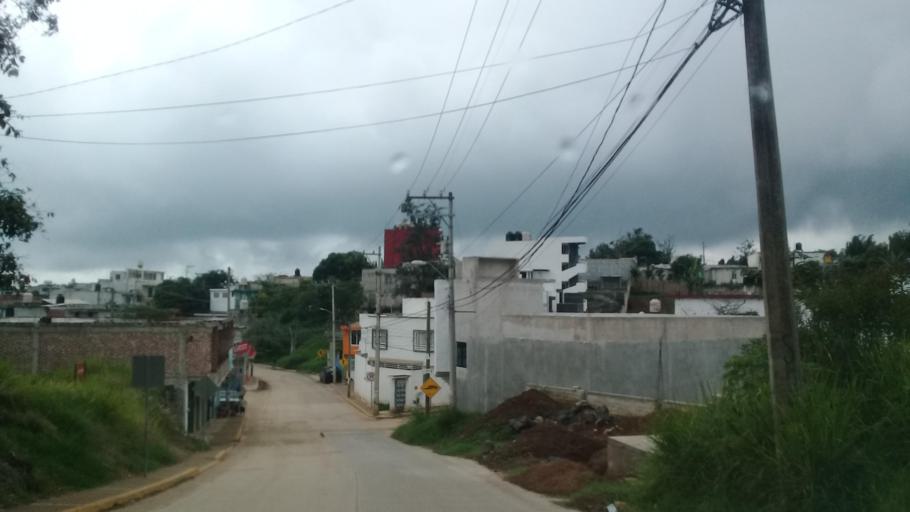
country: MX
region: Veracruz
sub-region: Emiliano Zapata
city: Las Trancas
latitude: 19.5015
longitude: -96.8702
